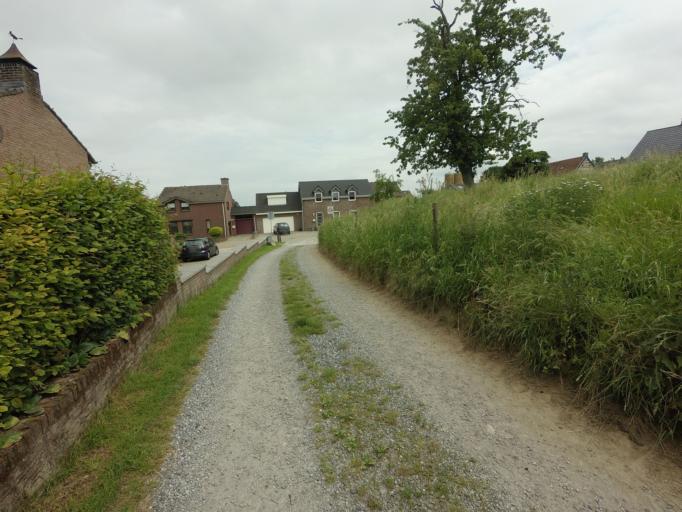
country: NL
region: Limburg
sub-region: Gemeente Simpelveld
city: Simpelveld
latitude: 50.8184
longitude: 5.9730
